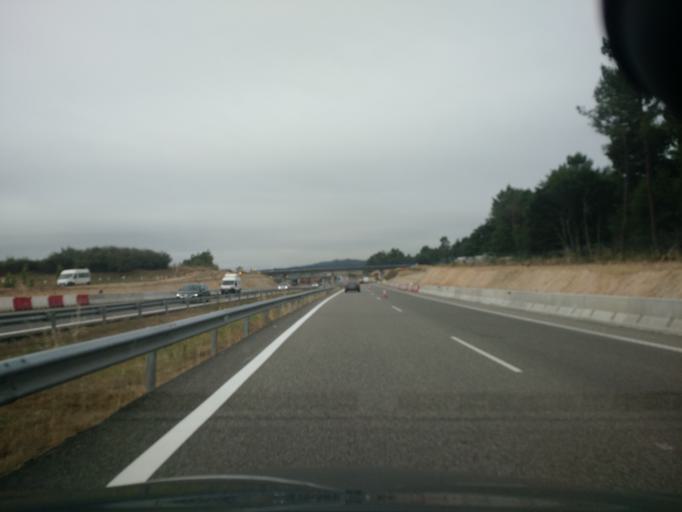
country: ES
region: Galicia
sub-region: Provincia da Coruna
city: Oroso
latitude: 42.9825
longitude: -8.4354
